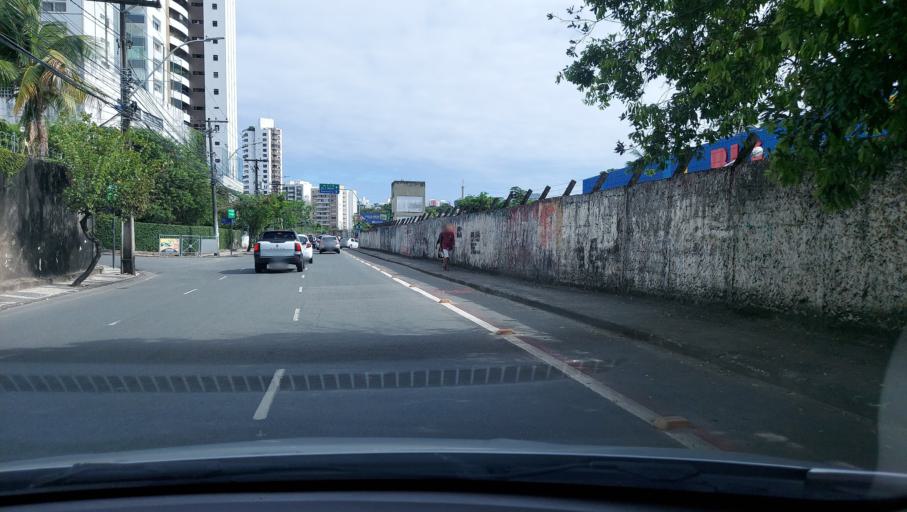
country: BR
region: Bahia
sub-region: Salvador
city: Salvador
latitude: -12.9853
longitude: -38.4638
